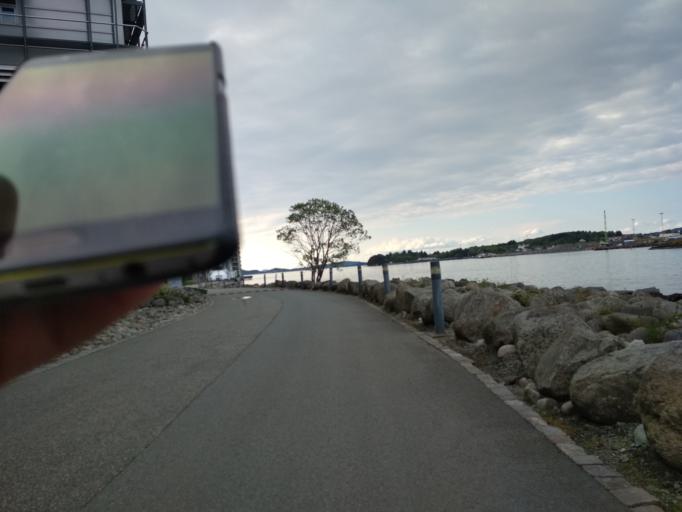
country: NO
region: Rogaland
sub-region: Stavanger
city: Stavanger
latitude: 58.9792
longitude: 5.7204
